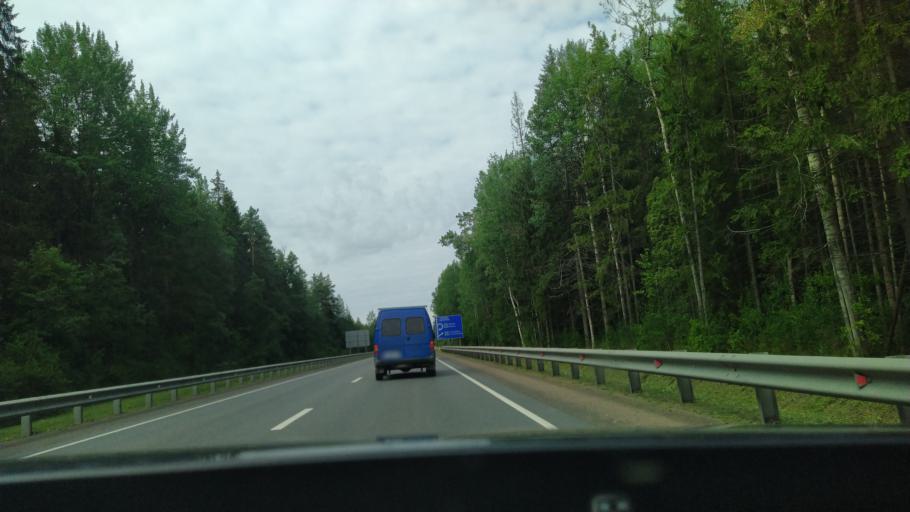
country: RU
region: Leningrad
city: Ul'yanovka
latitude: 59.6111
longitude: 30.7706
